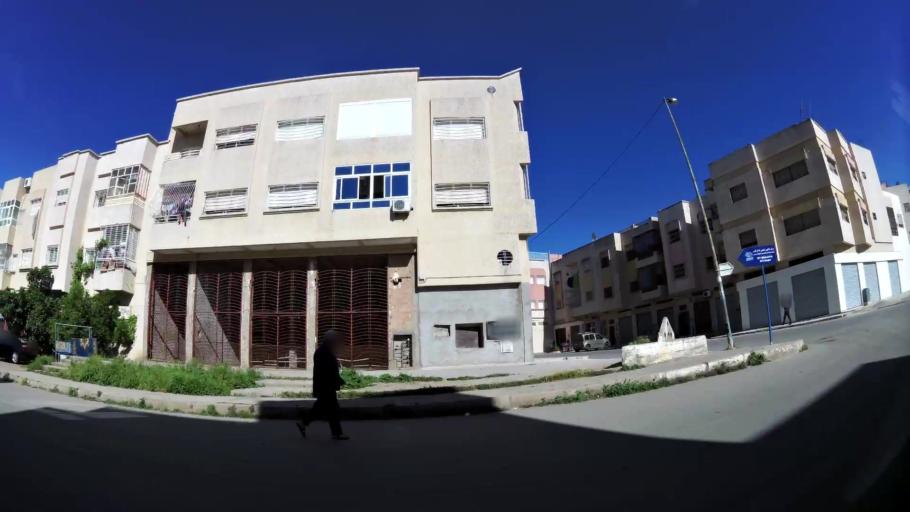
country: MA
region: Fes-Boulemane
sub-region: Fes
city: Fes
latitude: 34.0146
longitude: -4.9668
